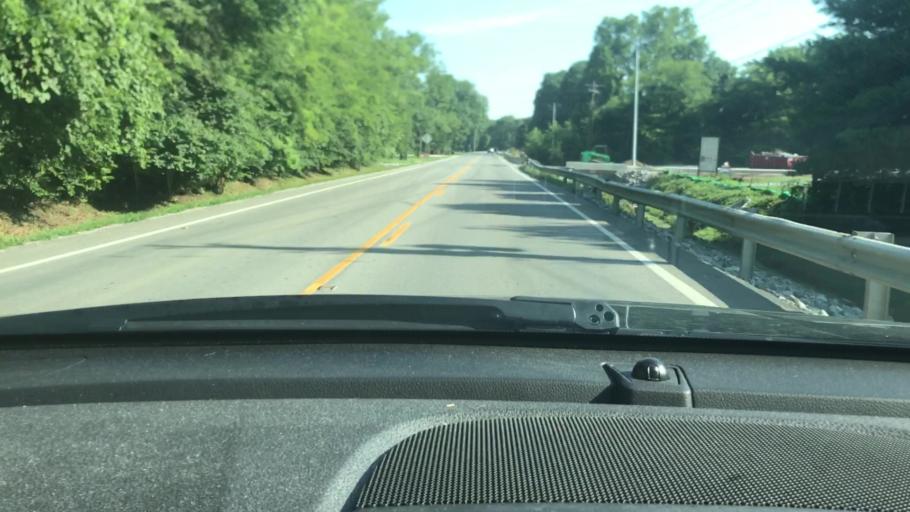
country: US
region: Tennessee
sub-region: Sumner County
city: Shackle Island
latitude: 36.3420
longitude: -86.6139
